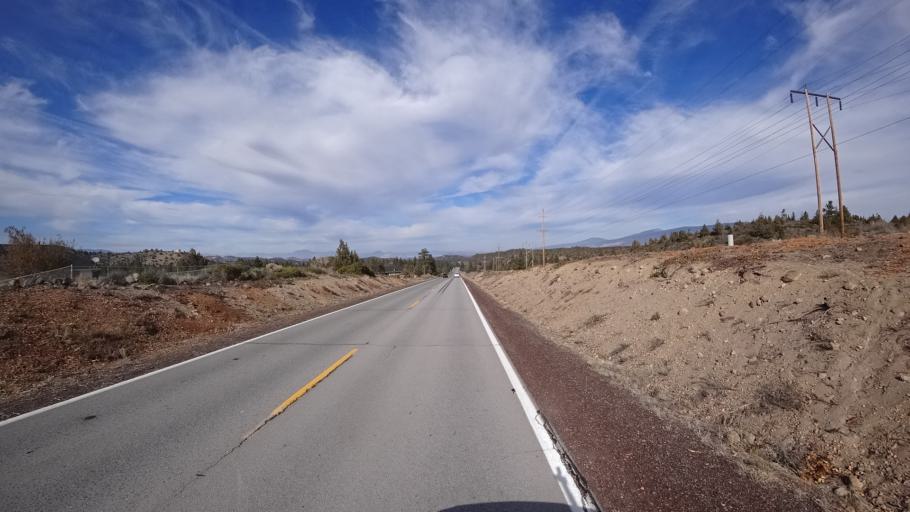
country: US
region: California
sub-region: Siskiyou County
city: Weed
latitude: 41.4989
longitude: -122.3630
